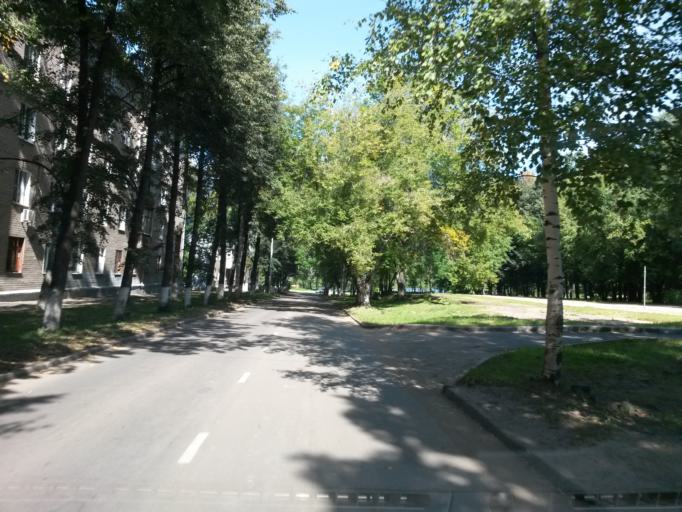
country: RU
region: Jaroslavl
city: Yaroslavl
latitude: 57.5815
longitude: 39.8476
